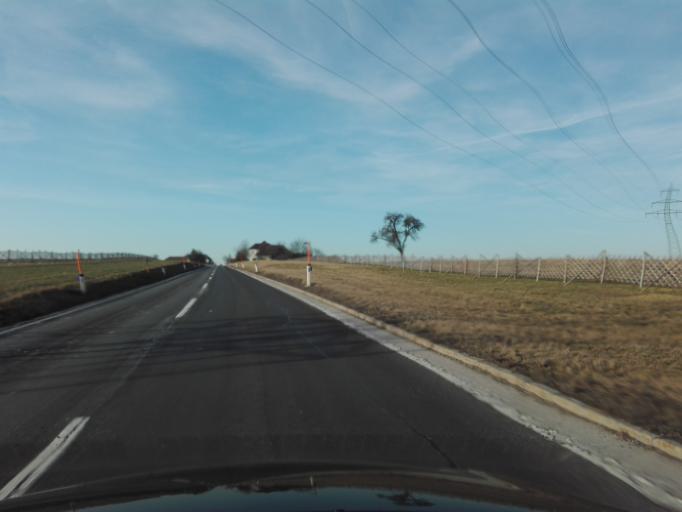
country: AT
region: Lower Austria
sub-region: Politischer Bezirk Amstetten
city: Strengberg
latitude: 48.1532
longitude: 14.6233
